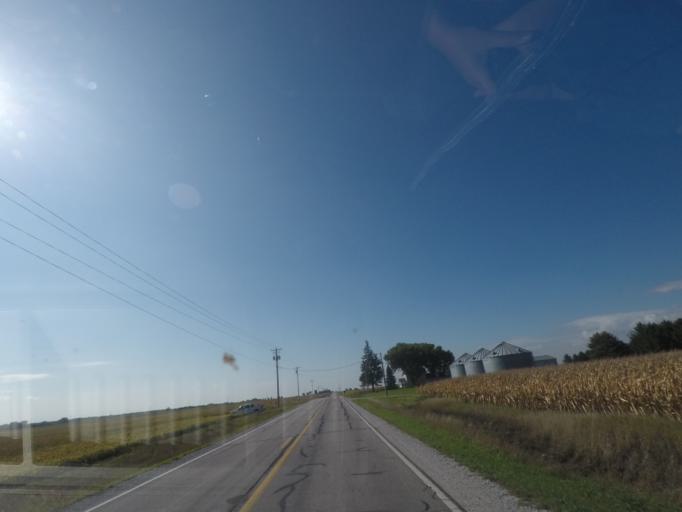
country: US
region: Iowa
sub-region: Story County
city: Nevada
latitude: 42.0415
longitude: -93.4058
